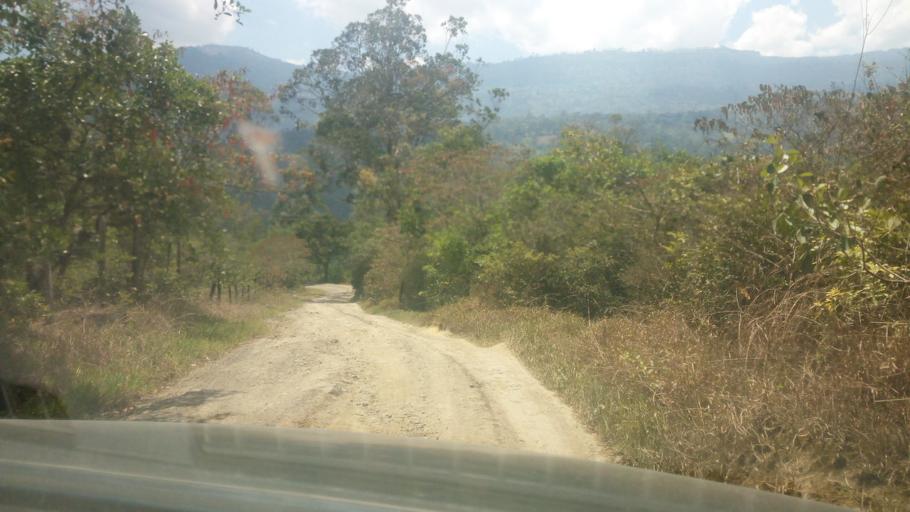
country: CO
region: Boyaca
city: Guateque
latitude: 4.9887
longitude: -73.4642
